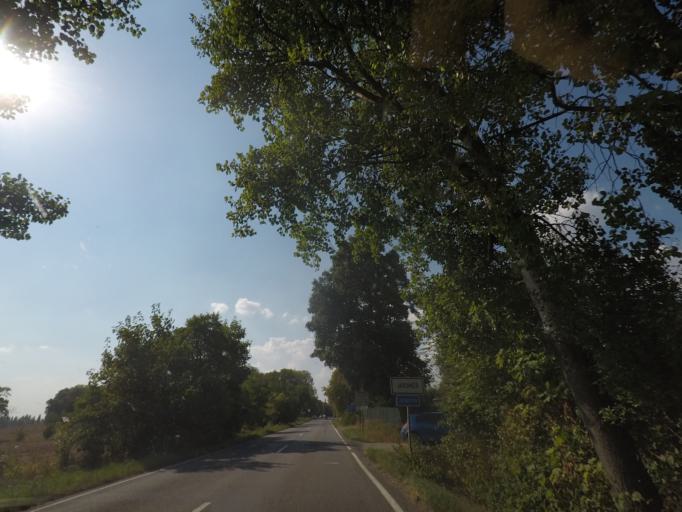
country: CZ
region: Kralovehradecky
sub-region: Okres Nachod
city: Jaromer
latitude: 50.3345
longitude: 15.9372
